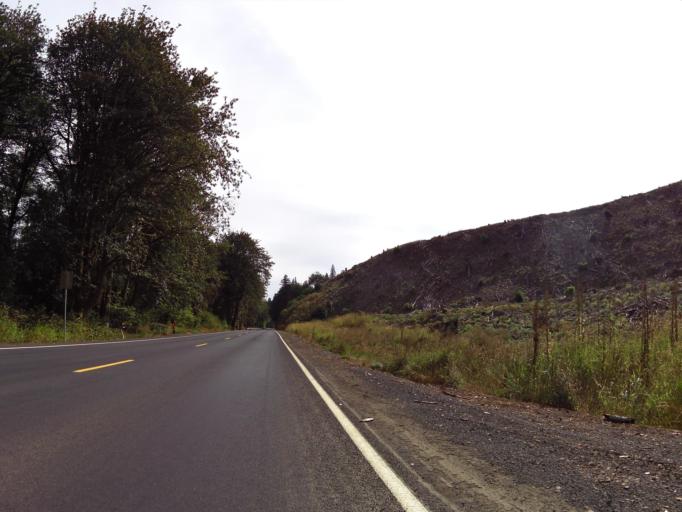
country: US
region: Washington
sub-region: Cowlitz County
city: Castle Rock
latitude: 46.3437
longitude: -122.9391
